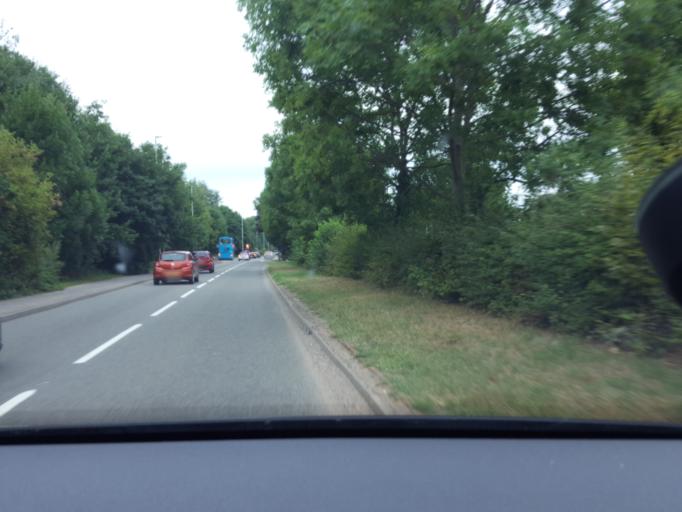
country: GB
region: England
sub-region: Leicestershire
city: Hathern
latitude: 52.7671
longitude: -1.2365
